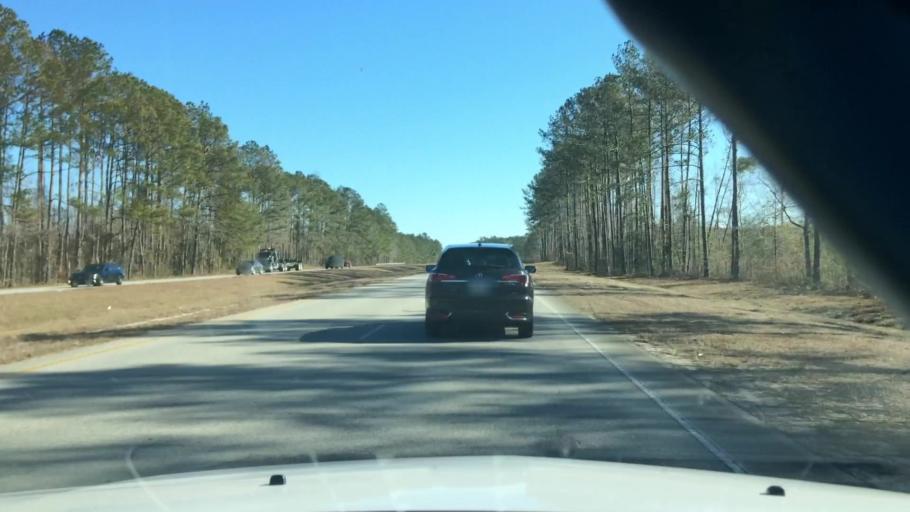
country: US
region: North Carolina
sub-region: Brunswick County
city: Bolivia
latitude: 34.0650
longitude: -78.1898
